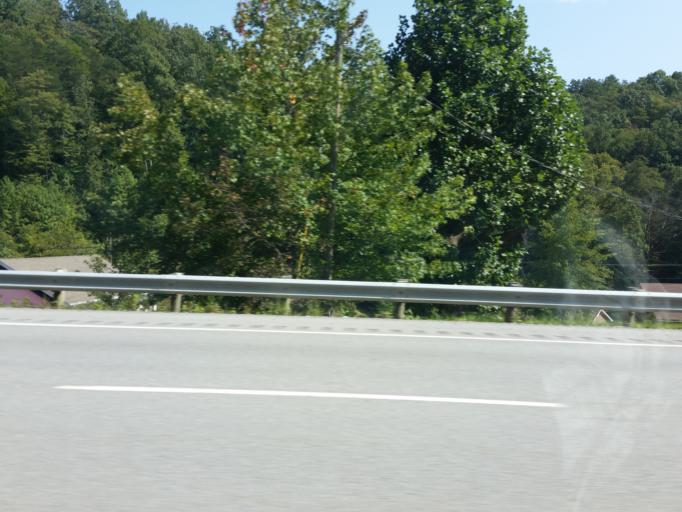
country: US
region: Kentucky
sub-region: Bell County
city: Pineville
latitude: 36.7752
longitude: -83.5880
